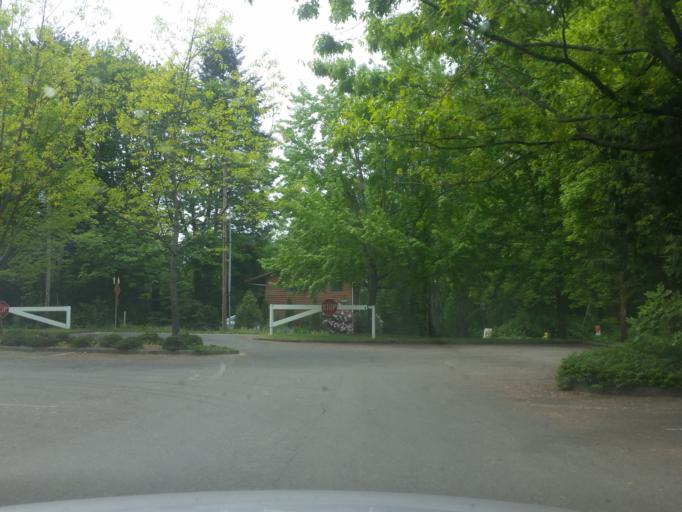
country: US
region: Washington
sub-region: King County
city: Kirkland
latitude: 47.6738
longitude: -122.1930
